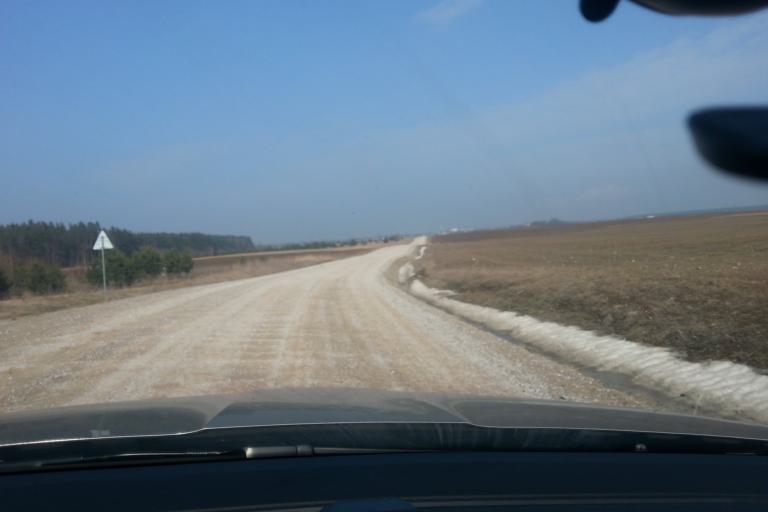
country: LT
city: Trakai
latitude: 54.5866
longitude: 24.9770
